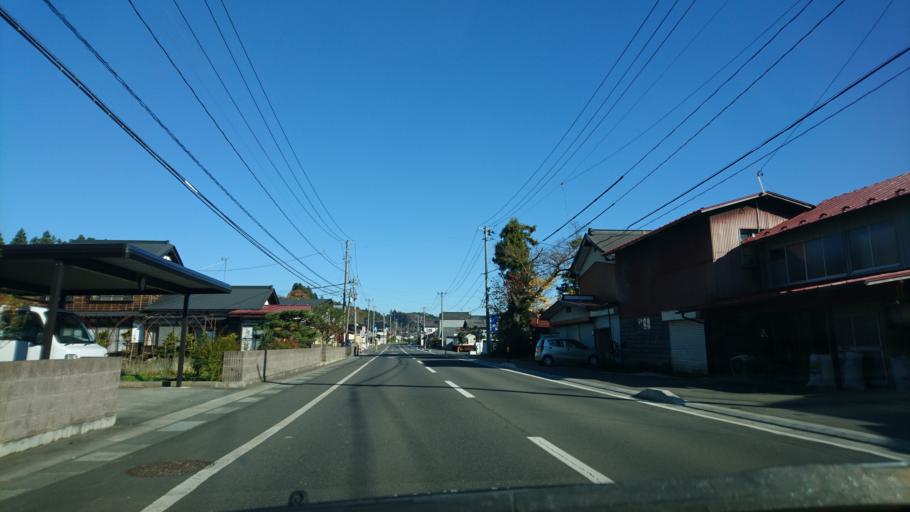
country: JP
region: Iwate
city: Mizusawa
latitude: 39.0663
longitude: 141.1275
